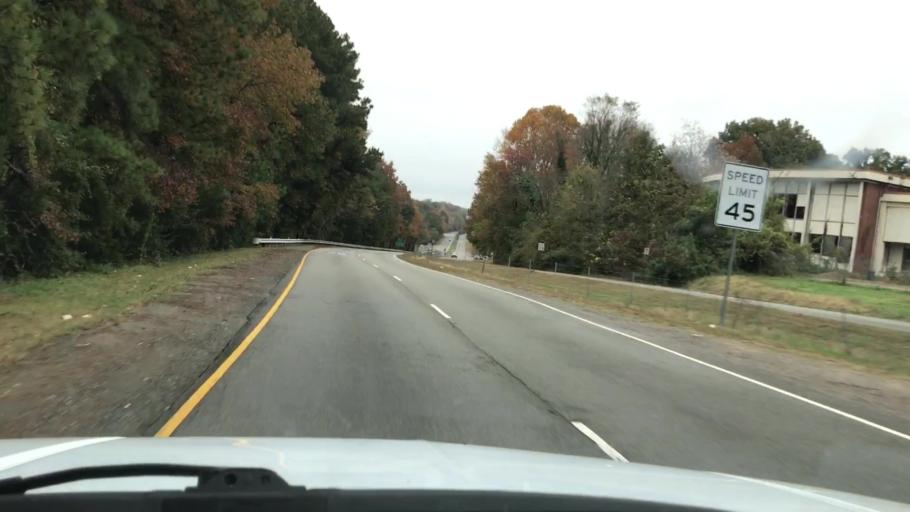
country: US
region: Virginia
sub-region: Henrico County
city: Chamberlayne
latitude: 37.6104
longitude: -77.4470
